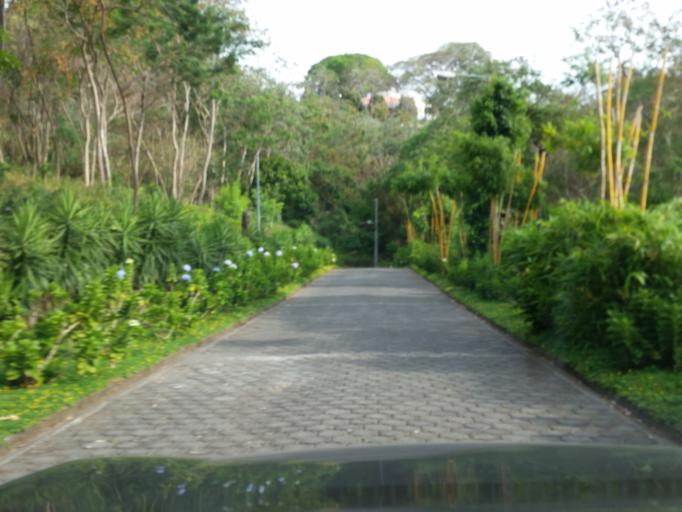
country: NI
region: Masaya
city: Ticuantepe
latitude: 12.0477
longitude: -86.2645
